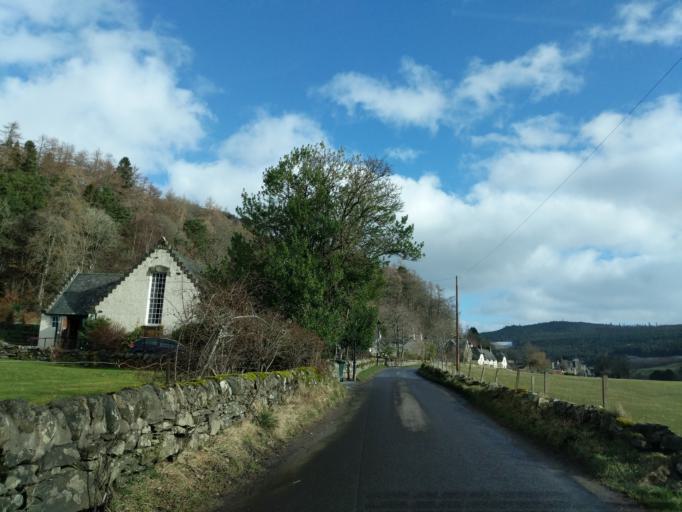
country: GB
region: Scotland
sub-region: Perth and Kinross
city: Aberfeldy
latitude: 56.5981
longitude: -4.0578
